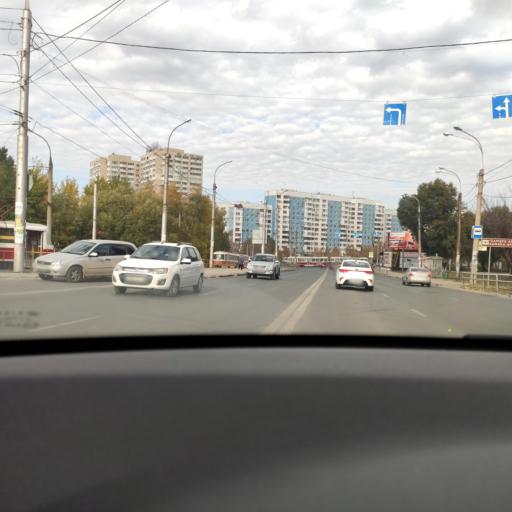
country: RU
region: Samara
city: Samara
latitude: 53.2595
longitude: 50.2166
